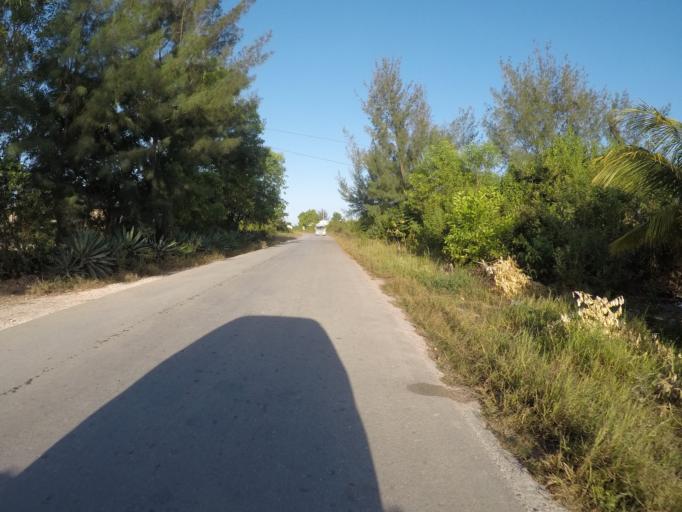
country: TZ
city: Kiwengwa
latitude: -6.1446
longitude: 39.4981
